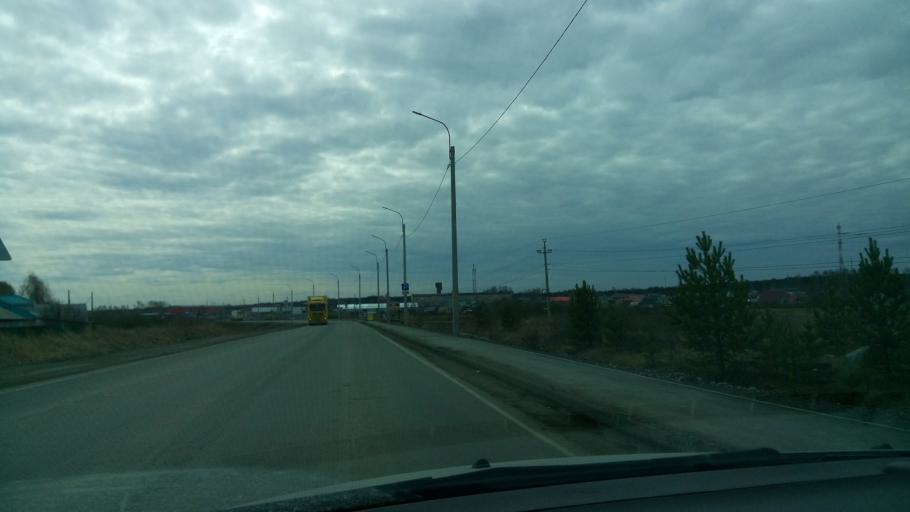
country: RU
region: Sverdlovsk
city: Verkhnyaya Pyshma
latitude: 56.9631
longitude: 60.6701
